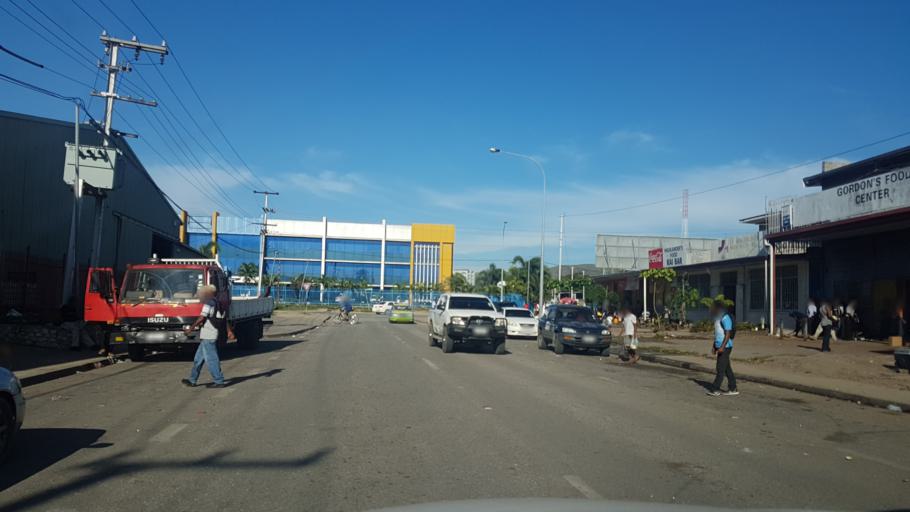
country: PG
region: National Capital
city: Port Moresby
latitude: -9.4507
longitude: 147.1909
